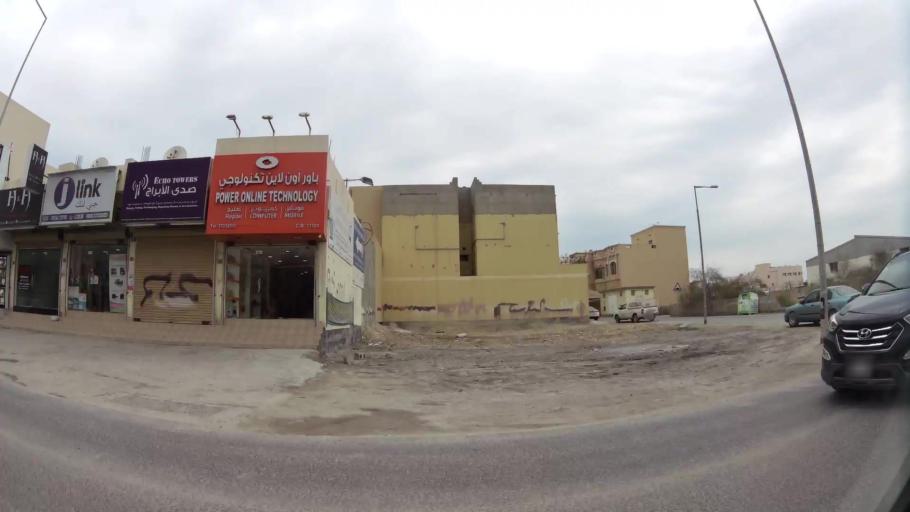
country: BH
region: Northern
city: Sitrah
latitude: 26.1668
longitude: 50.6125
